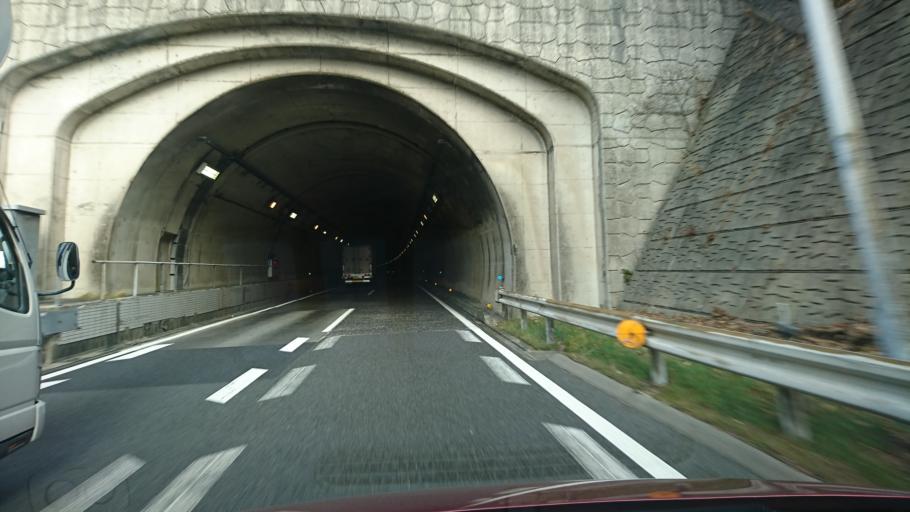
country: JP
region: Hyogo
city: Kariya
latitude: 34.7888
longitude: 134.2146
